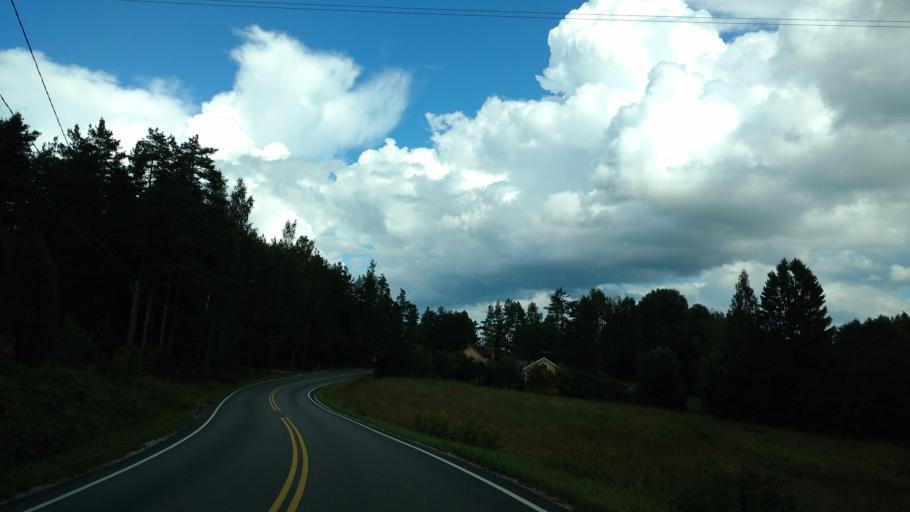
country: FI
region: Uusimaa
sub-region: Helsinki
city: Karjalohja
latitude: 60.2142
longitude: 23.6779
